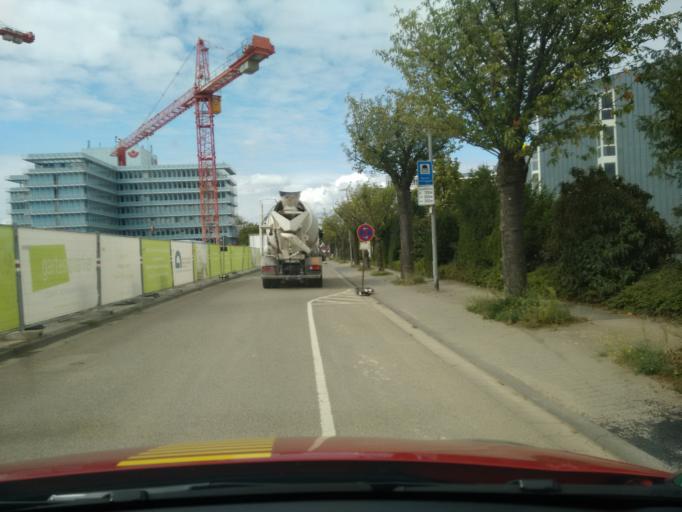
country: DE
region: Rheinland-Pfalz
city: Mainz
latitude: 49.9809
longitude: 8.2899
